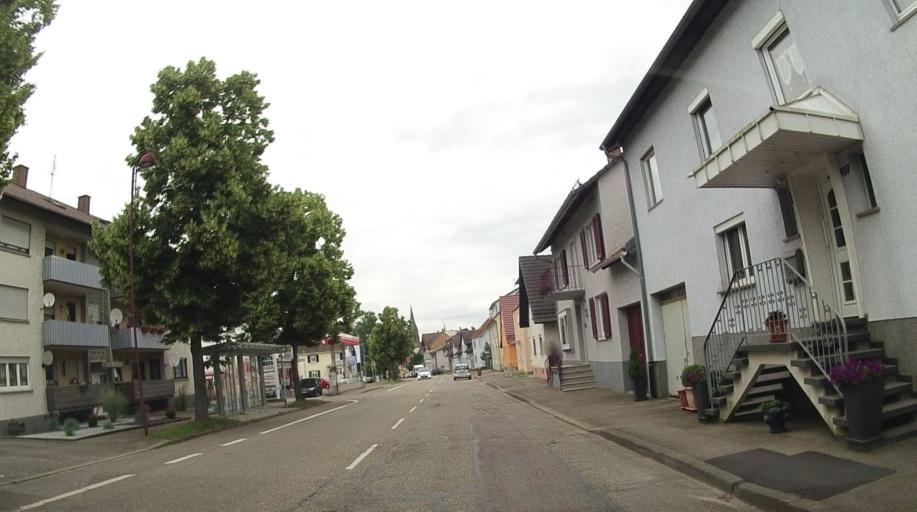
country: DE
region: Baden-Wuerttemberg
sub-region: Karlsruhe Region
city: Kuppenheim
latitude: 48.8240
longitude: 8.2524
